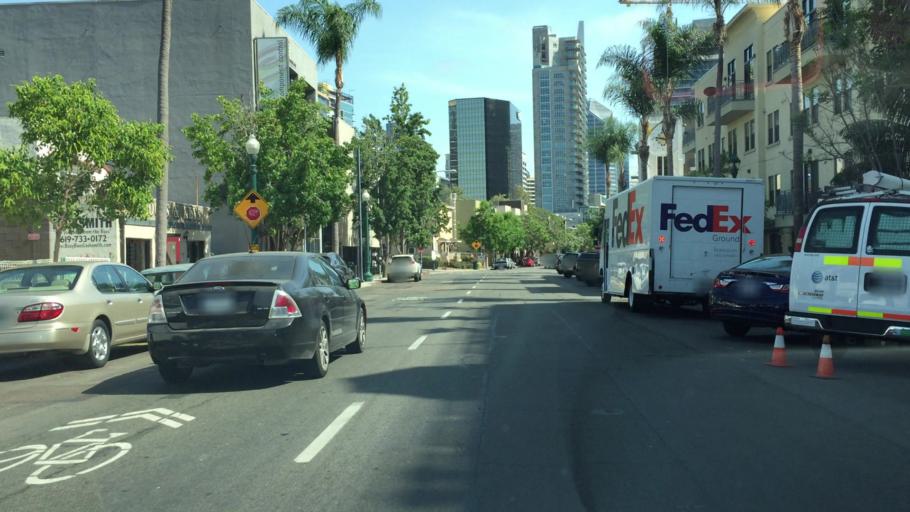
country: US
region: California
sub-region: San Diego County
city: San Diego
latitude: 32.7239
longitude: -117.1693
